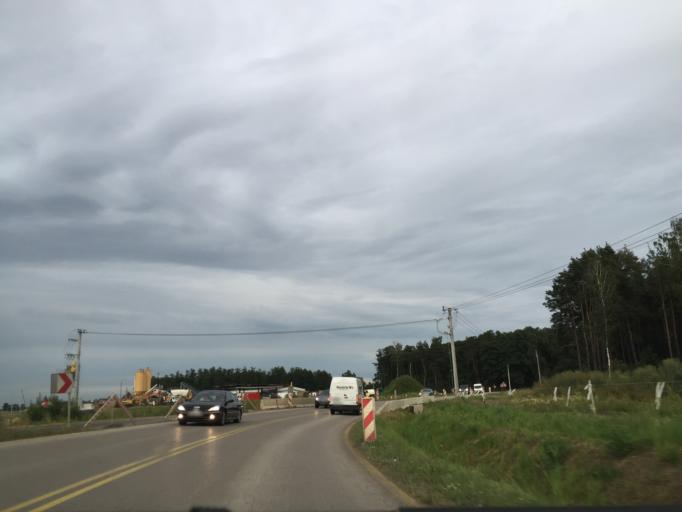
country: PL
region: Podlasie
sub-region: Powiat zambrowski
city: Rutki-Kossaki
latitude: 53.1092
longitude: 22.5848
